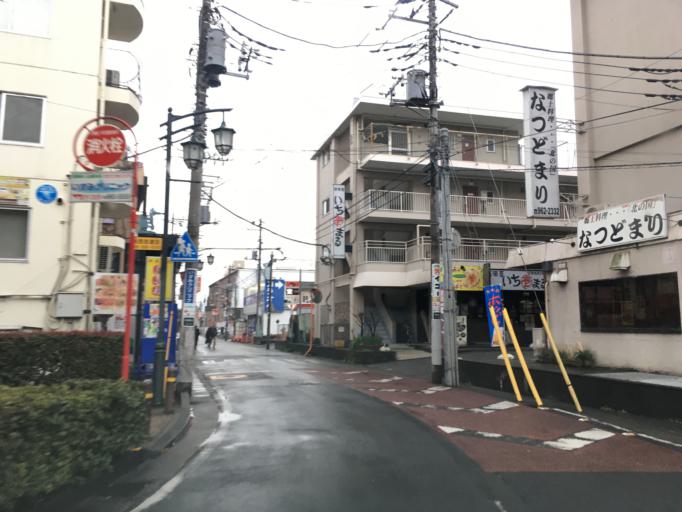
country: JP
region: Saitama
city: Koshigaya
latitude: 35.8767
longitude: 139.7904
